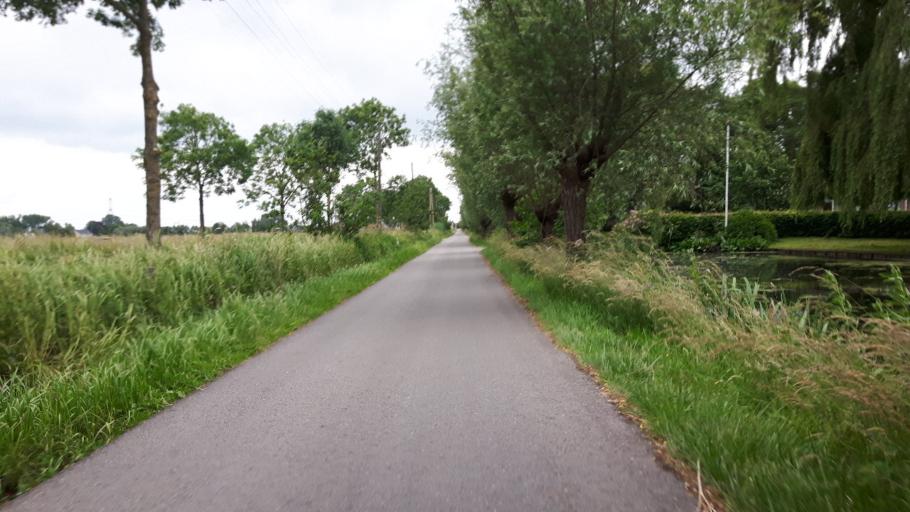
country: NL
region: Utrecht
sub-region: Gemeente Oudewater
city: Oudewater
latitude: 52.0516
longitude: 4.8483
